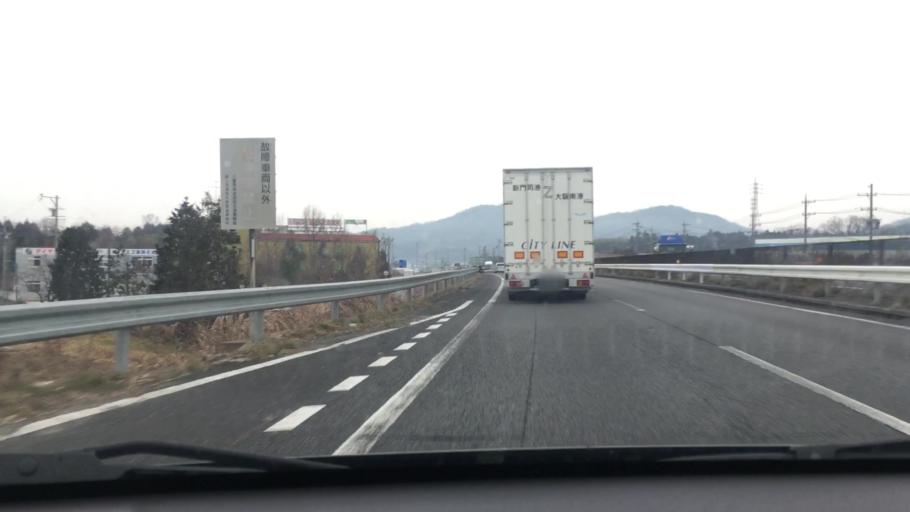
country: JP
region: Mie
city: Ueno-ebisumachi
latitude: 34.7613
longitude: 136.1533
